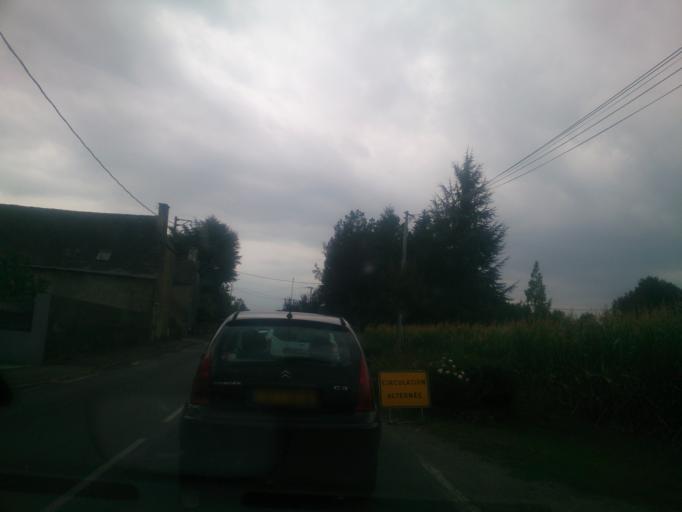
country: FR
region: Midi-Pyrenees
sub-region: Departement des Hautes-Pyrenees
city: Horgues
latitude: 43.1856
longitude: 0.0891
